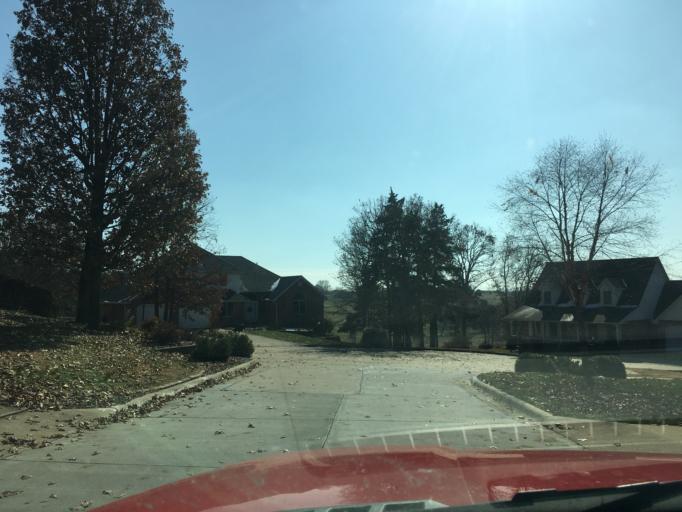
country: US
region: Missouri
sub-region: Cole County
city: Wardsville
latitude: 38.4812
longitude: -92.1793
